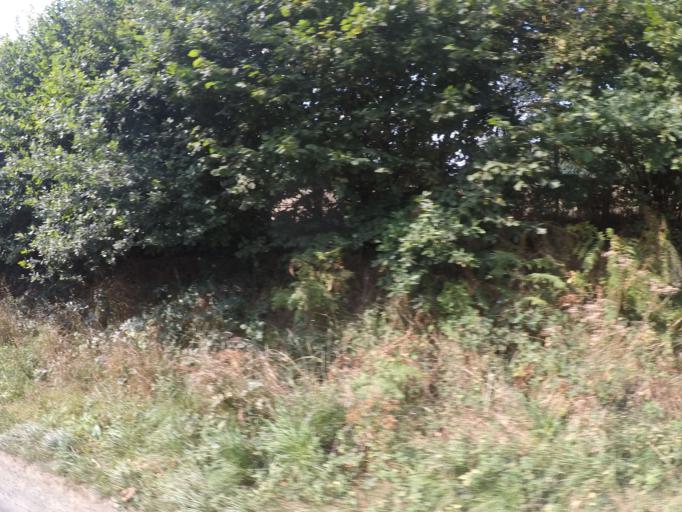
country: FR
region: Brittany
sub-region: Departement des Cotes-d'Armor
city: Tremuson
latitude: 48.5423
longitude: -2.8909
